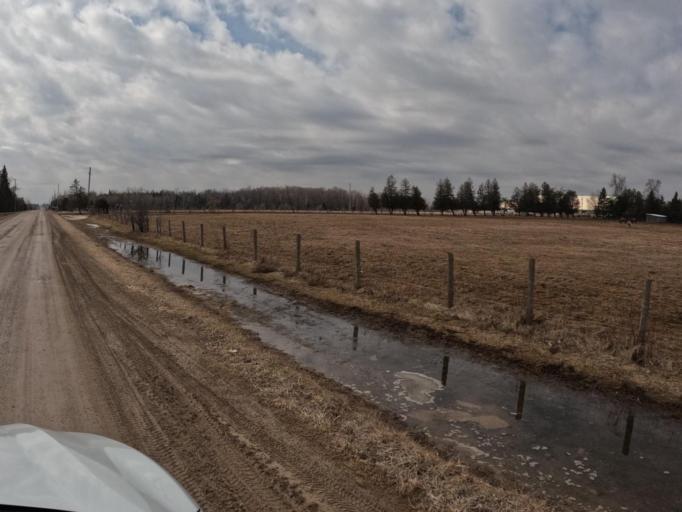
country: CA
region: Ontario
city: Orangeville
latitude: 43.9339
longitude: -80.2210
